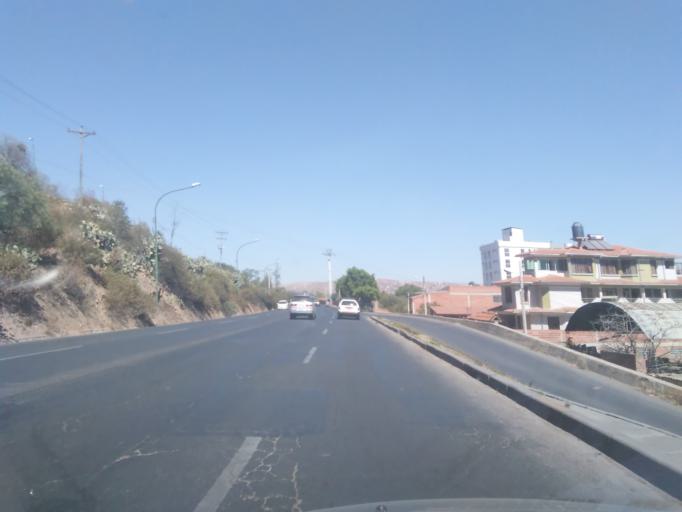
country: BO
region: Cochabamba
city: Cochabamba
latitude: -17.3861
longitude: -66.1411
